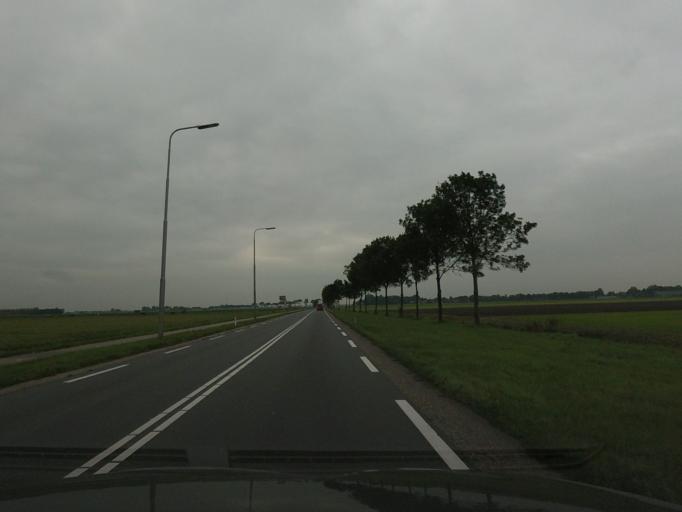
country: NL
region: North Holland
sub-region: Gemeente Hoorn
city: Hoorn
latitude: 52.6945
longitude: 5.0248
